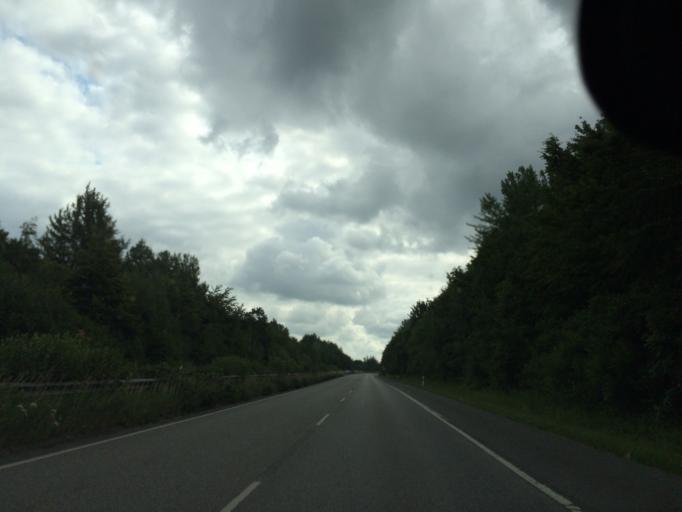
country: DE
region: Schleswig-Holstein
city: Kronshagen
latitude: 54.3518
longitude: 10.1084
